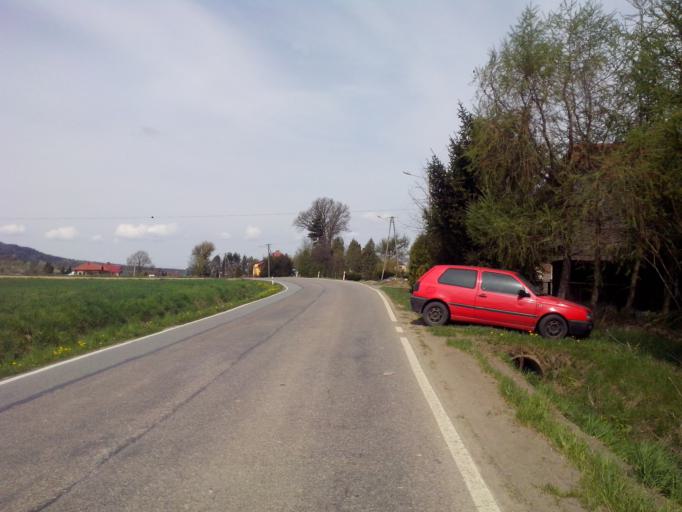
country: PL
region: Subcarpathian Voivodeship
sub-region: Powiat strzyzowski
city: Jawornik
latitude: 49.8070
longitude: 21.8553
